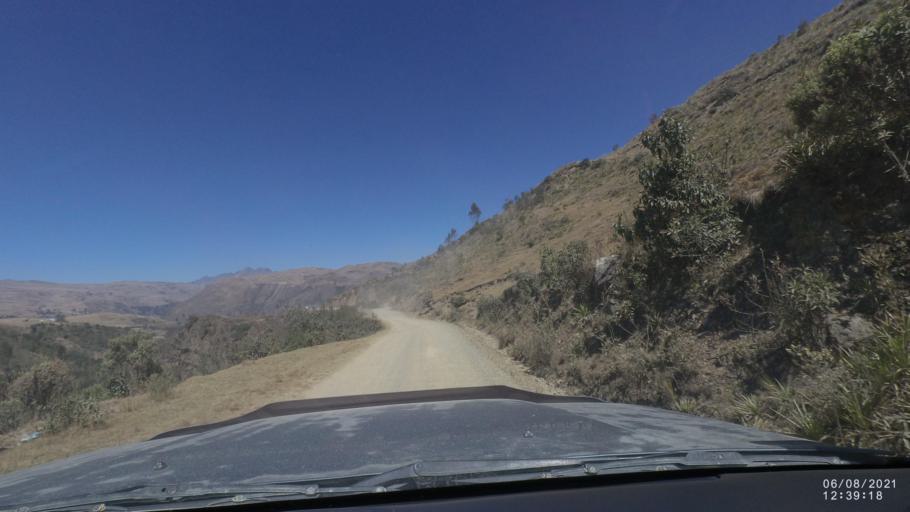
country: BO
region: Cochabamba
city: Colchani
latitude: -16.7791
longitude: -66.6624
